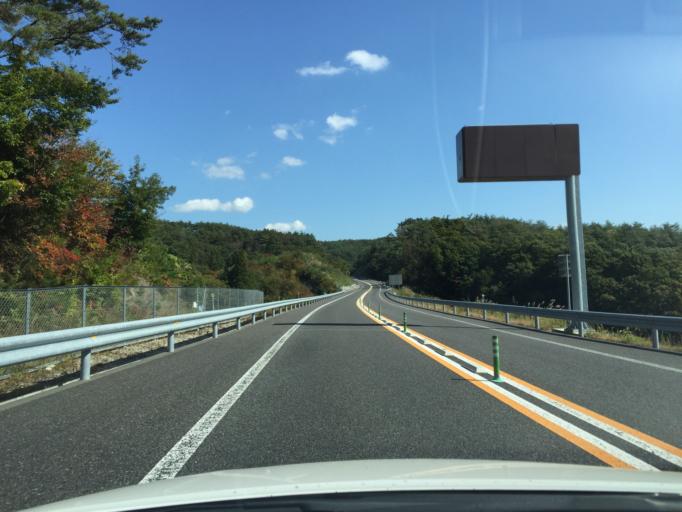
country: JP
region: Fukushima
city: Ishikawa
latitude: 37.2035
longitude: 140.4830
